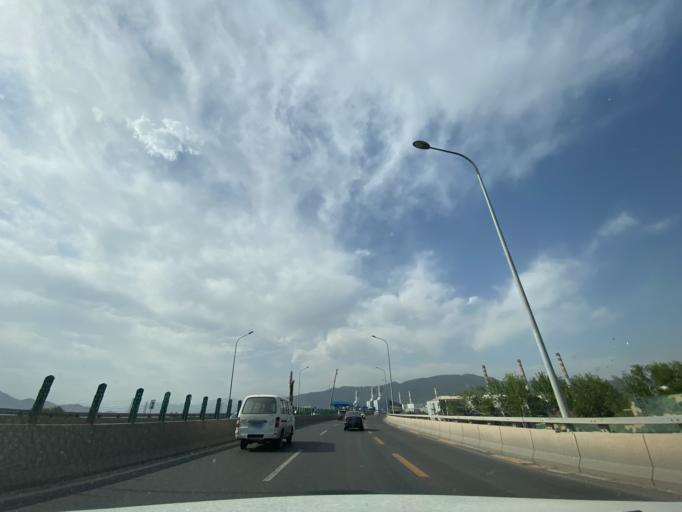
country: CN
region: Beijing
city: Guangning
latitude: 39.9329
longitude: 116.1263
